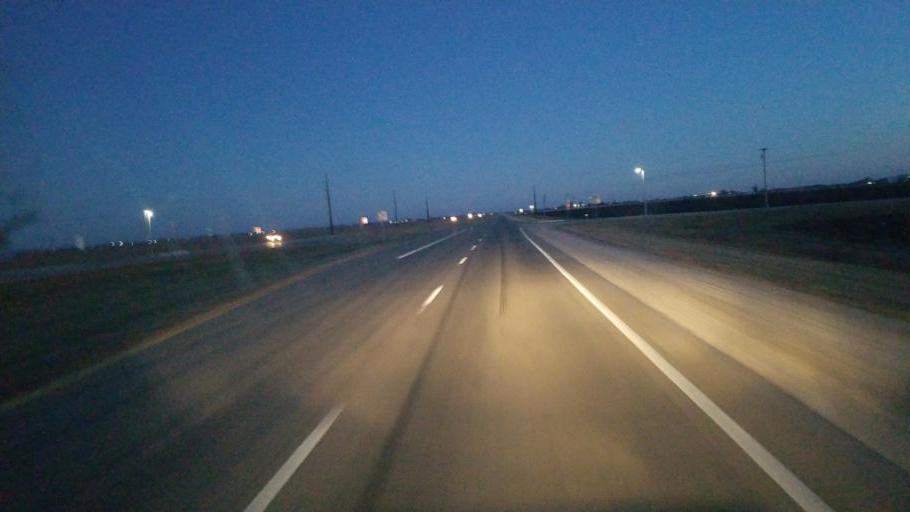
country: US
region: Iowa
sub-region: Henry County
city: New London
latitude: 40.8552
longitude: -91.3279
